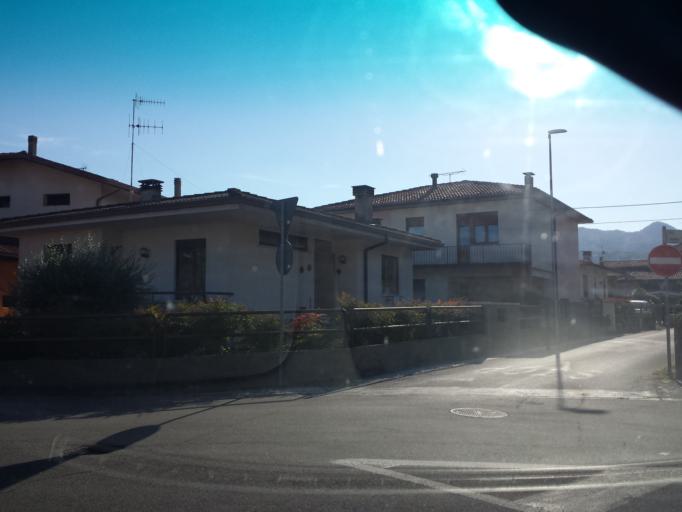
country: IT
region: Veneto
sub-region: Provincia di Vicenza
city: San Vito di Leguzzano
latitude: 45.6858
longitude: 11.3779
